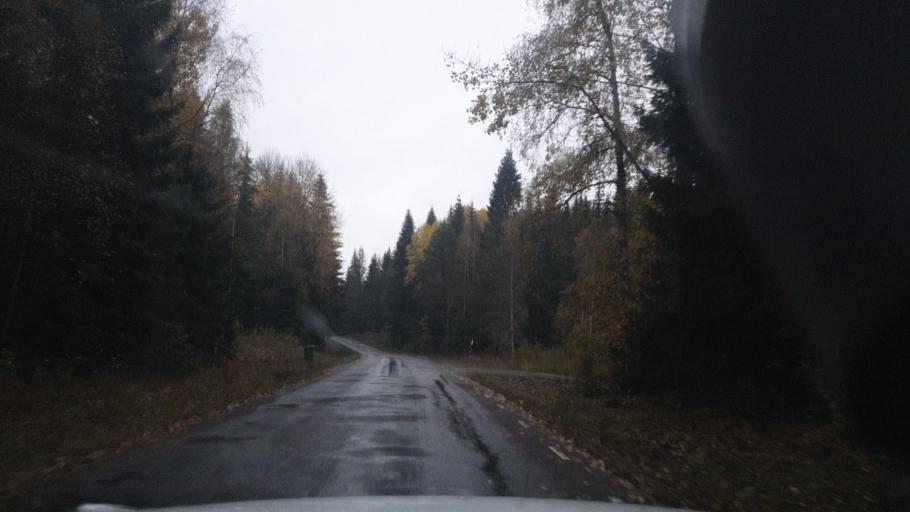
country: SE
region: Vaermland
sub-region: Eda Kommun
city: Amotfors
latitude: 59.8429
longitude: 12.4266
